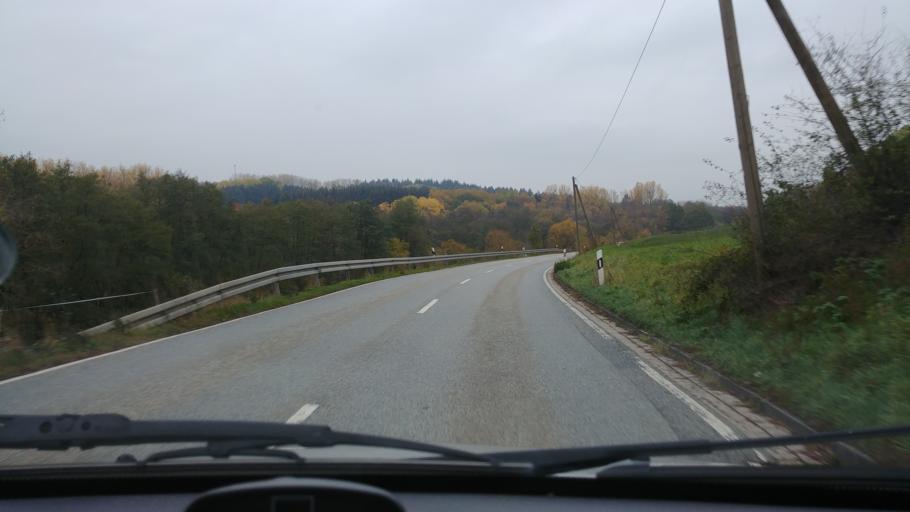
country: DE
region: Rheinland-Pfalz
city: Gemunden
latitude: 50.5371
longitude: 8.0375
